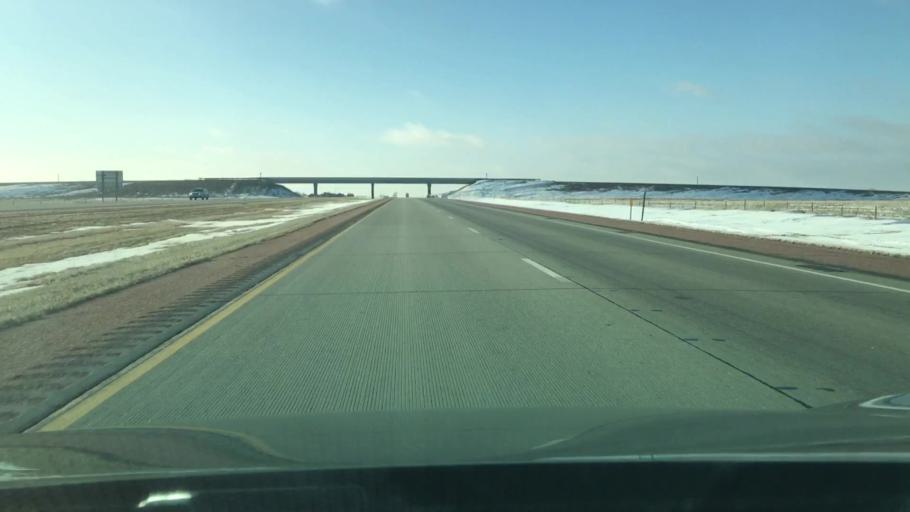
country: US
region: South Dakota
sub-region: Aurora County
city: Plankinton
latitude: 43.7083
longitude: -98.6520
